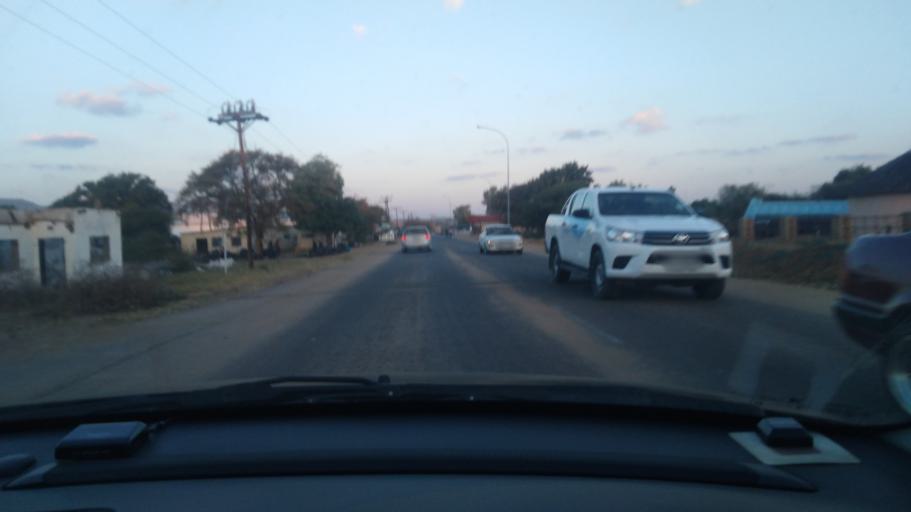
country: BW
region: Central
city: Mahalapye
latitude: -23.1038
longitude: 26.8306
